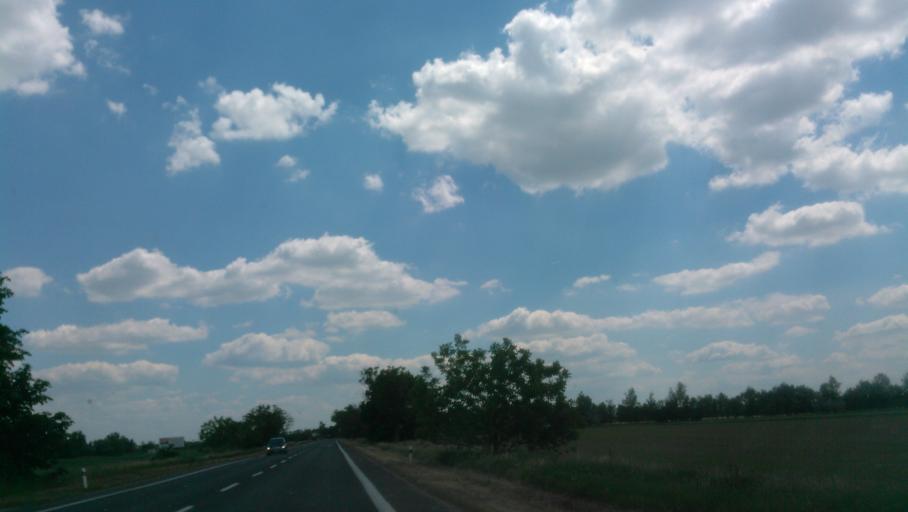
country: SK
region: Trnavsky
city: Samorin
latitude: 48.0476
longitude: 17.2932
